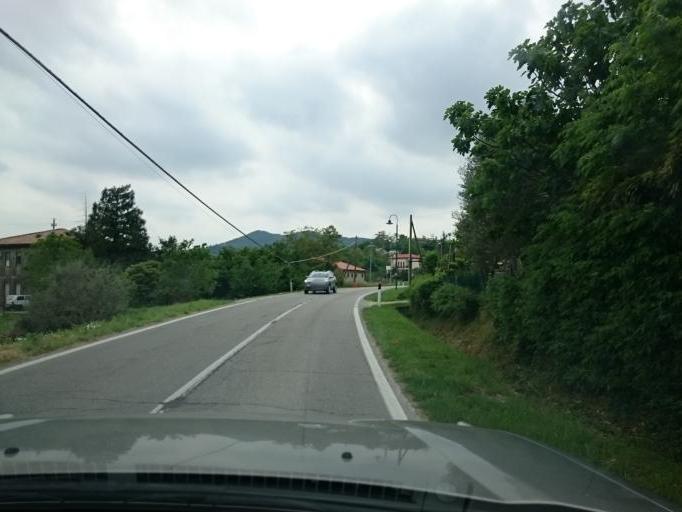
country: IT
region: Veneto
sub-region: Provincia di Padova
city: Arqua Petrarca
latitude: 45.2584
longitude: 11.7181
